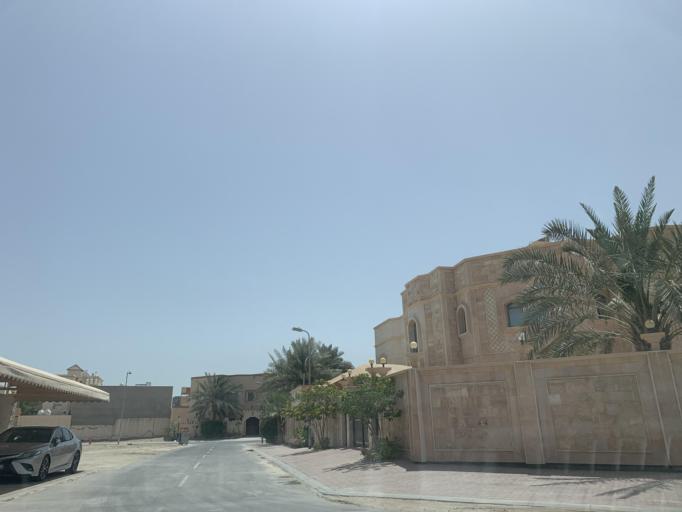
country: BH
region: Northern
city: Madinat `Isa
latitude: 26.1587
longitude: 50.5808
